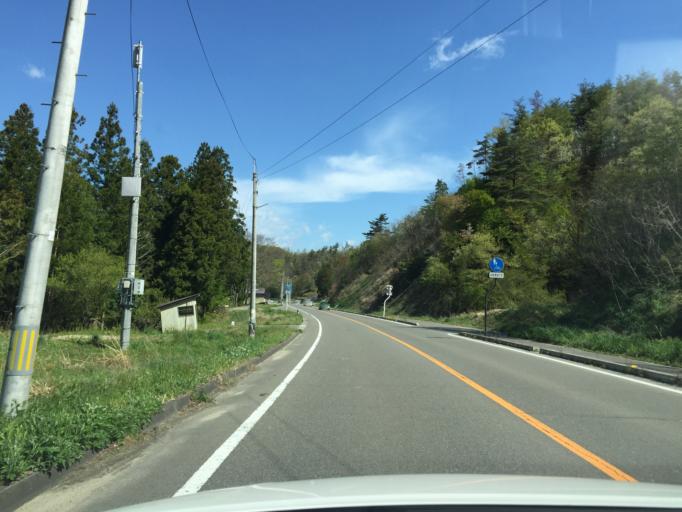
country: JP
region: Fukushima
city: Funehikimachi-funehiki
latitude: 37.5395
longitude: 140.5359
